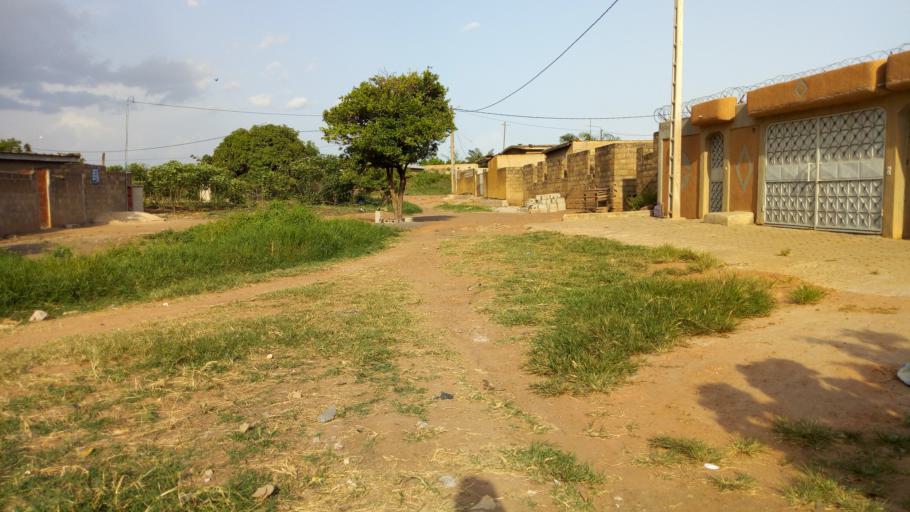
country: CI
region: Vallee du Bandama
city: Bouake
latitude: 7.7091
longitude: -5.0488
